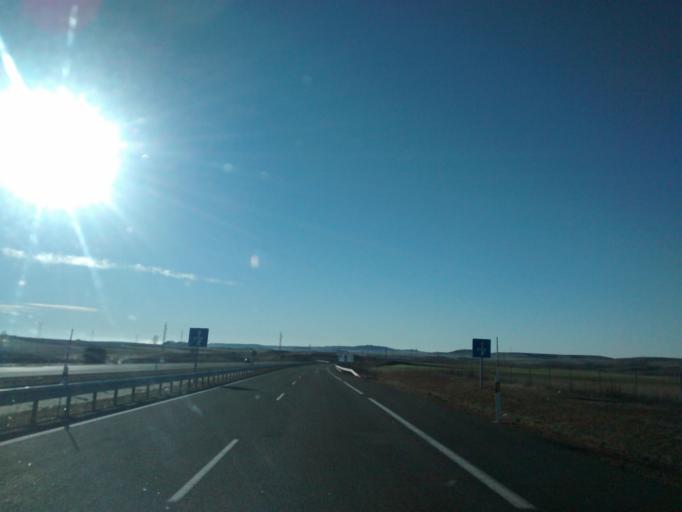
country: ES
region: Castille and Leon
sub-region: Provincia de Palencia
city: Herrera de Pisuerga
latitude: 42.6205
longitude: -4.3508
